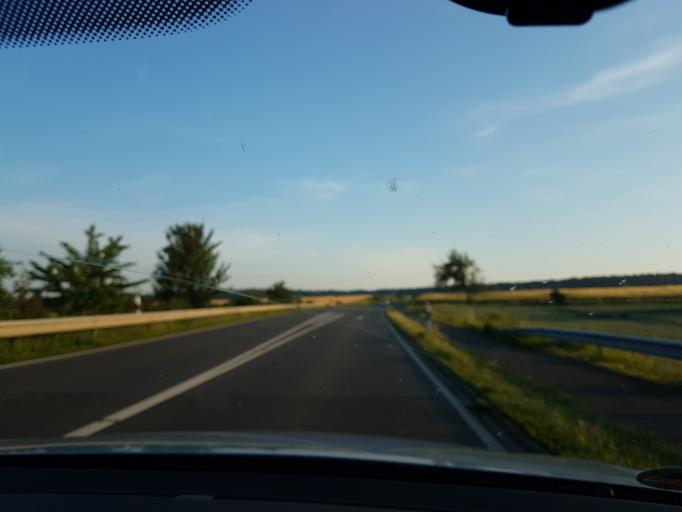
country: DE
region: Lower Saxony
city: Wolsdorf
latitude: 52.1942
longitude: 10.9691
